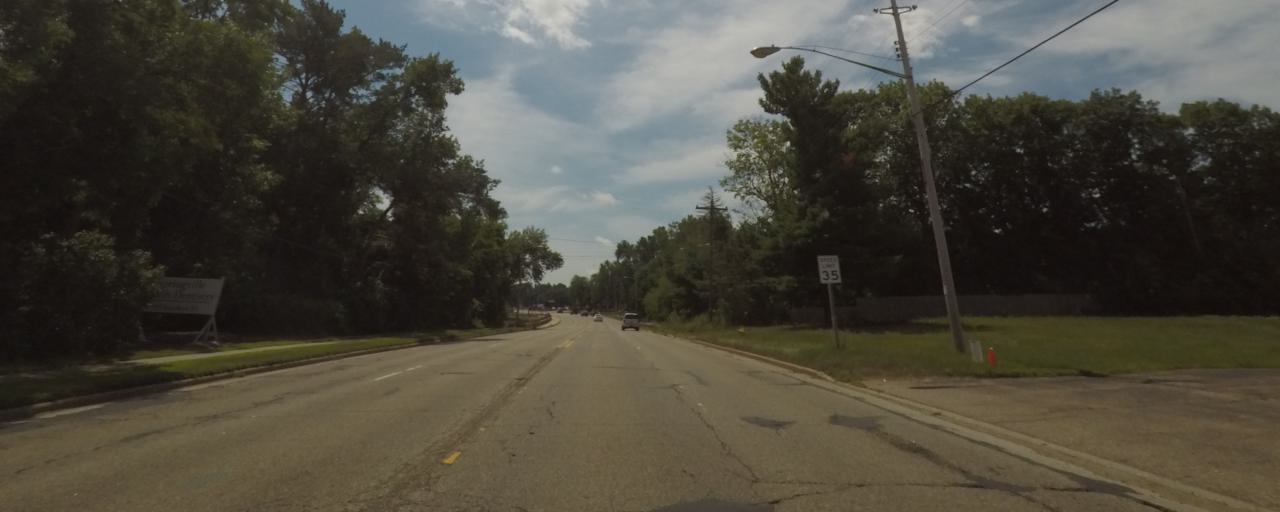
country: US
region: Wisconsin
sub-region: Portage County
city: Plover
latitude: 44.4733
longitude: -89.5476
